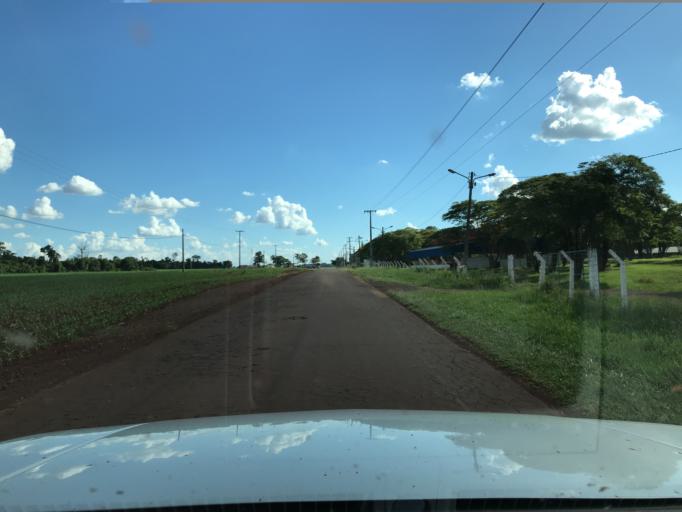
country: BR
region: Parana
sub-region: Palotina
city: Palotina
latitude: -24.2704
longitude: -53.8064
